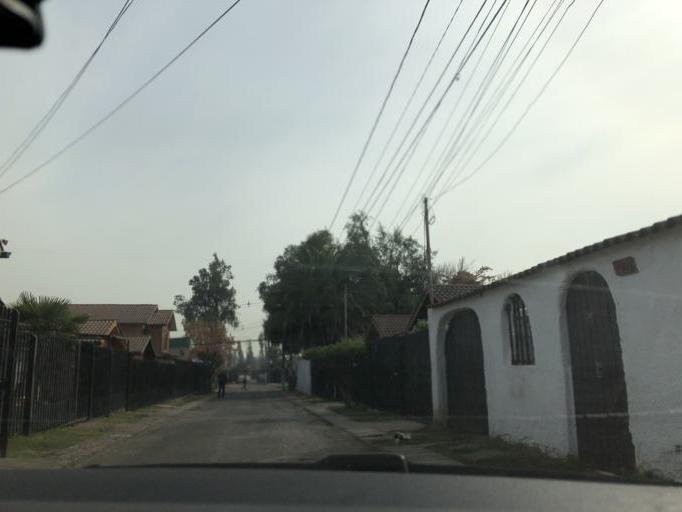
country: CL
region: Santiago Metropolitan
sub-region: Provincia de Cordillera
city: Puente Alto
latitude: -33.5498
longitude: -70.5633
